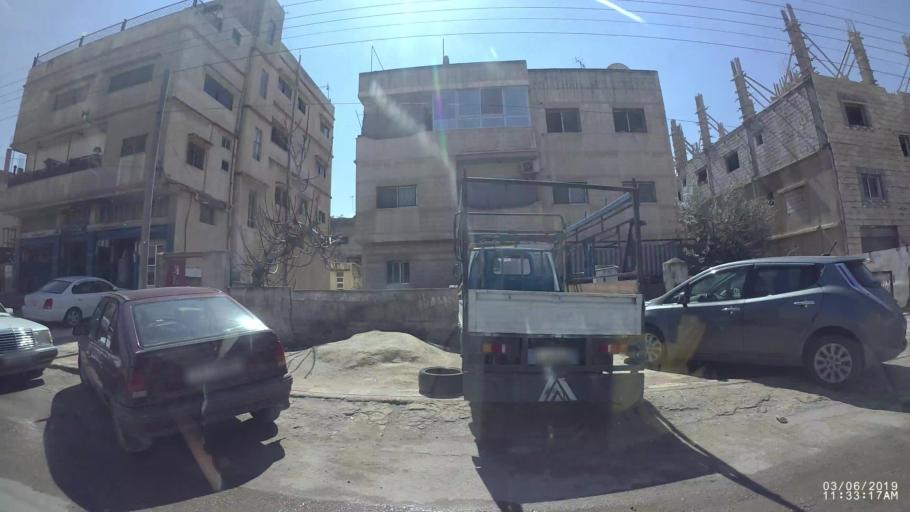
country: JO
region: Amman
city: Amman
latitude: 31.9803
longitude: 35.9956
